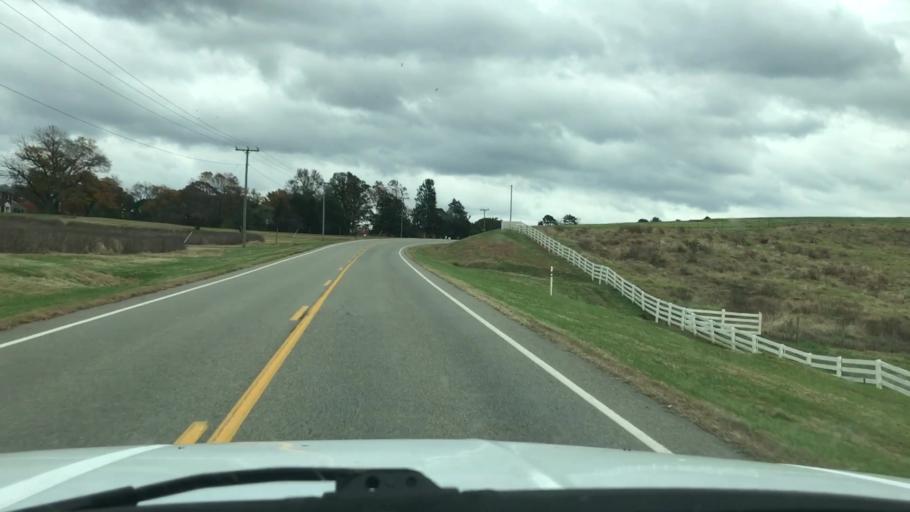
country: US
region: Virginia
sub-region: Goochland County
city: Goochland
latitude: 37.6464
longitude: -77.8210
